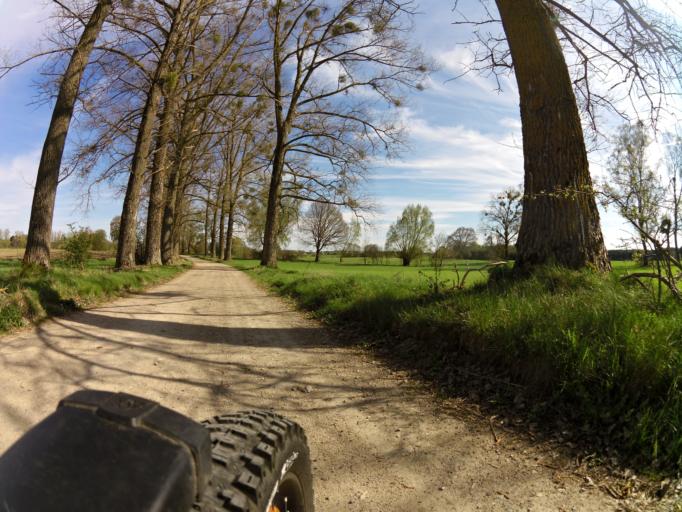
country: PL
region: West Pomeranian Voivodeship
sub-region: Powiat lobeski
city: Resko
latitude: 53.7907
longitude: 15.4791
